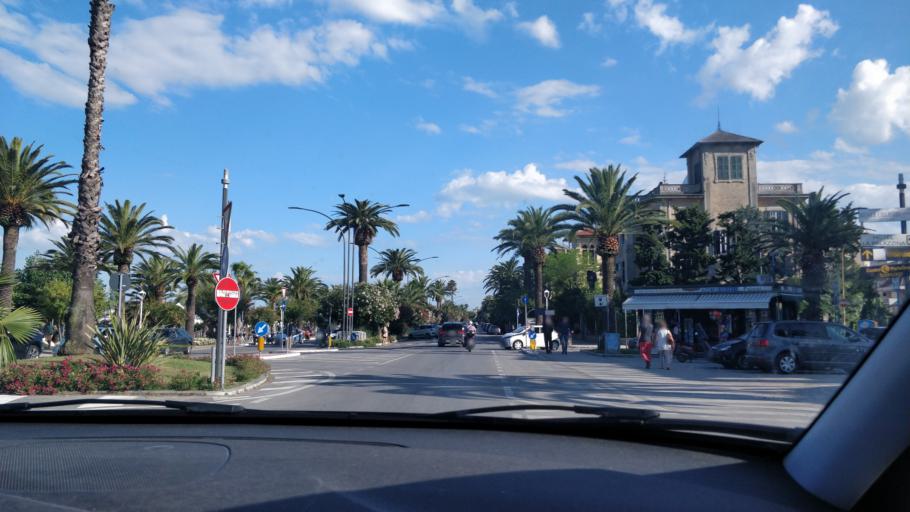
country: IT
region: The Marches
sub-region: Provincia di Ascoli Piceno
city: Grottammare
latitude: 42.9493
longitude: 13.8862
